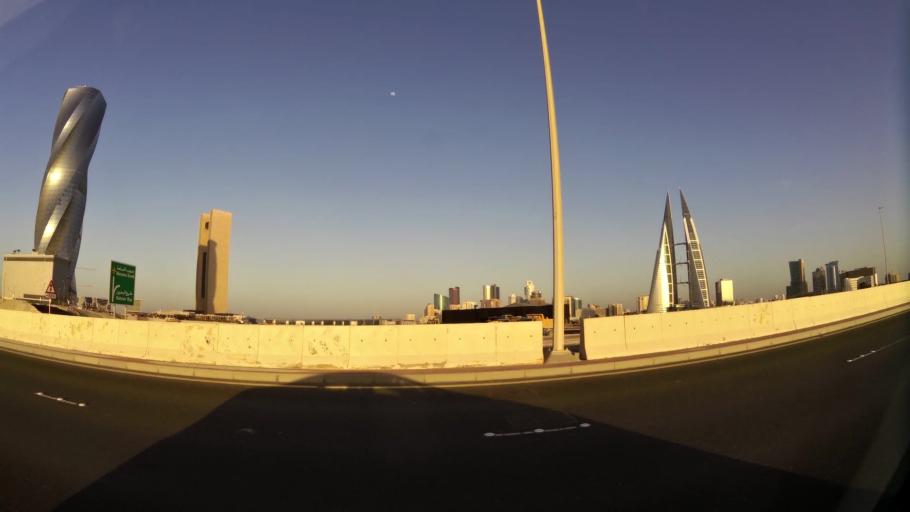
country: BH
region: Manama
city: Manama
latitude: 26.2437
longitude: 50.5743
